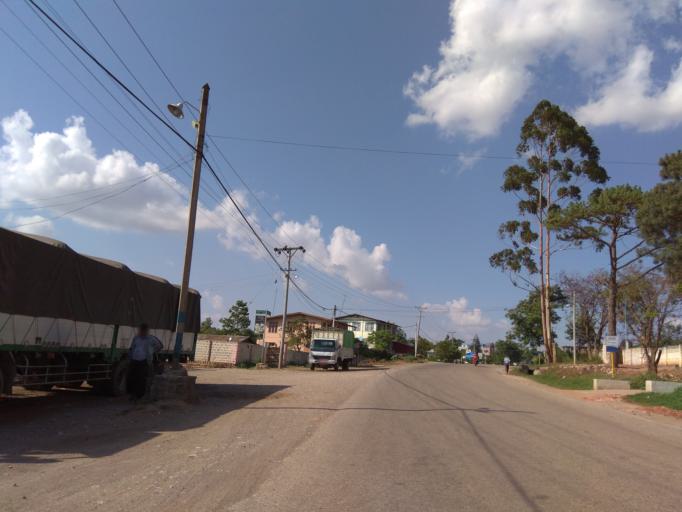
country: MM
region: Shan
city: Taunggyi
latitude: 20.6591
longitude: 96.6431
